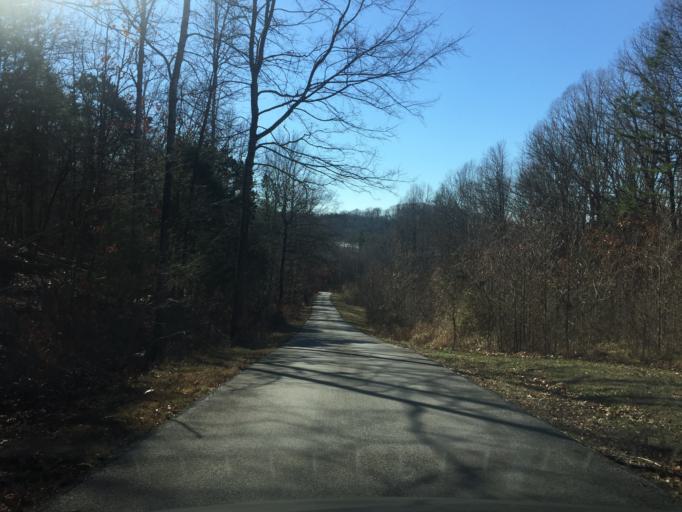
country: US
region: Tennessee
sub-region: Hamilton County
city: Harrison
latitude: 35.0814
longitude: -85.1266
